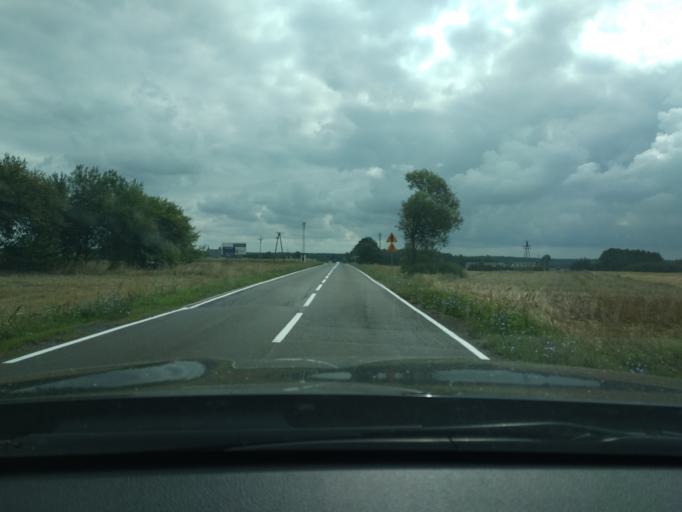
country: PL
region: Masovian Voivodeship
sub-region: Powiat pultuski
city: Obryte
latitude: 52.6540
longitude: 21.2336
